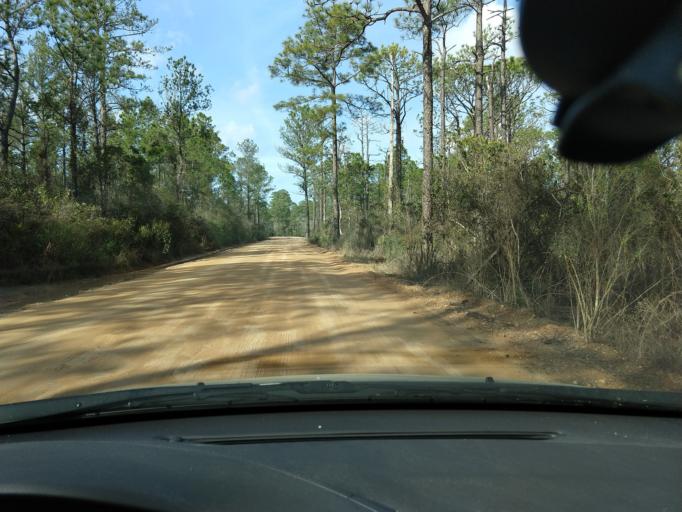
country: US
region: Florida
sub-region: Walton County
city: Seaside
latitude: 30.3672
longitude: -86.1285
